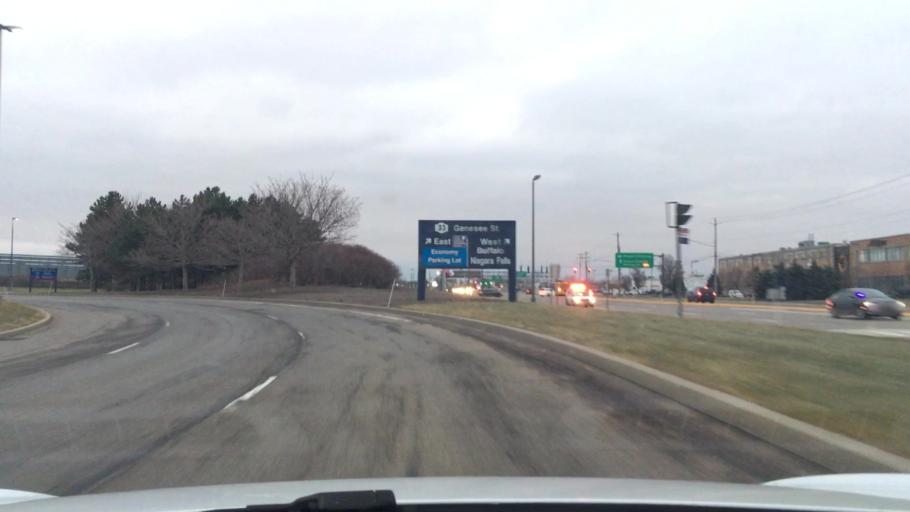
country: US
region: New York
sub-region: Erie County
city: Williamsville
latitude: 42.9333
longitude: -78.7241
